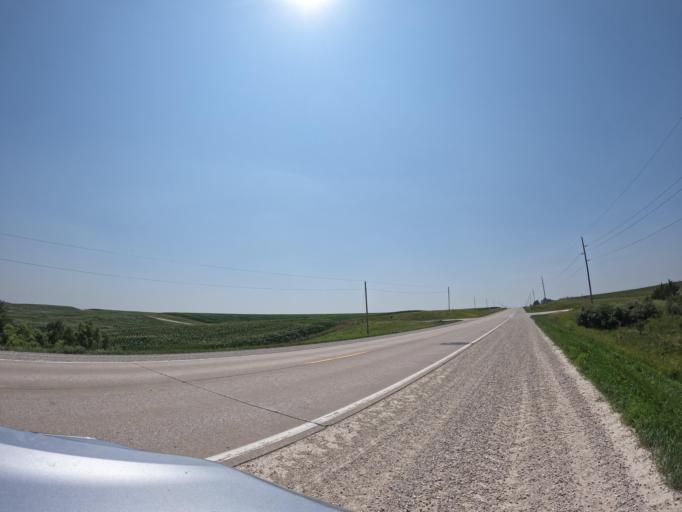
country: US
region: Iowa
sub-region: Keokuk County
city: Sigourney
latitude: 41.3369
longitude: -92.2564
